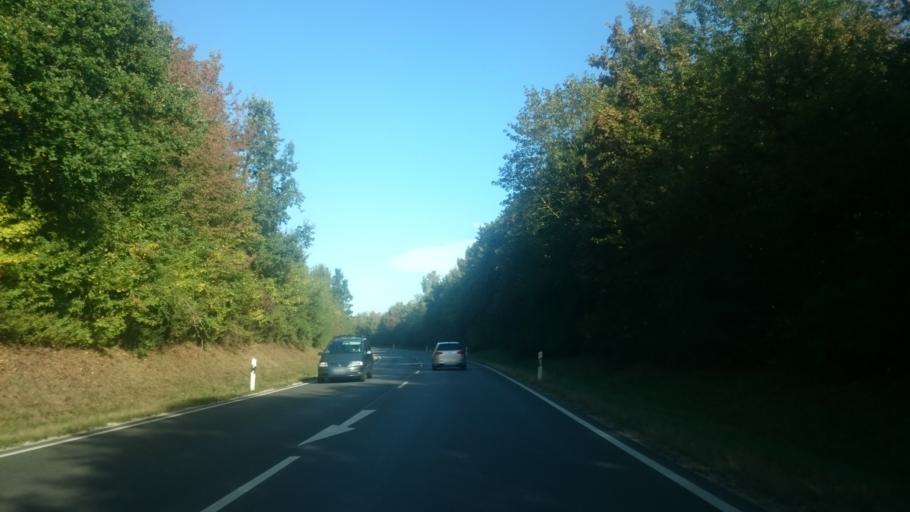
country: DE
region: Bavaria
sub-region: Regierungsbezirk Mittelfranken
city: Weissenburg in Bayern
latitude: 49.0339
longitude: 10.9881
